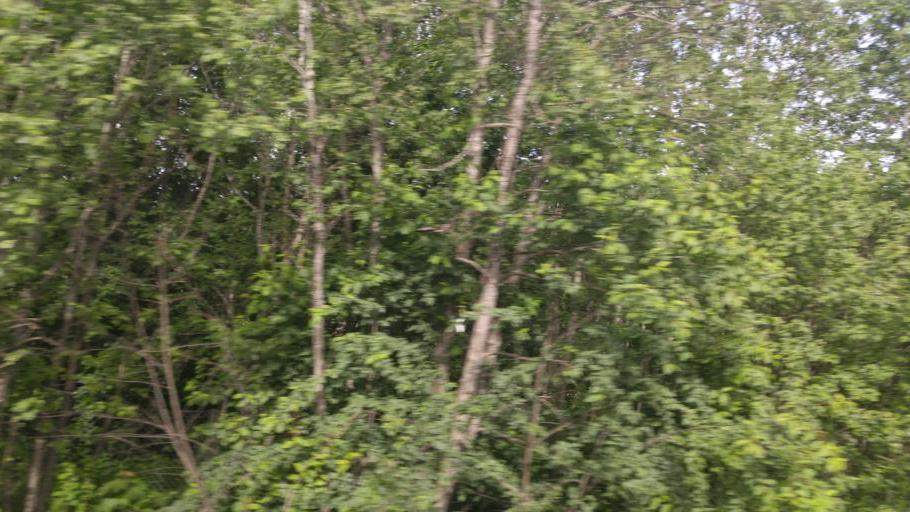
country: NO
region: Sor-Trondelag
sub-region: Trondheim
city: Trondheim
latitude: 63.3842
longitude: 10.3572
